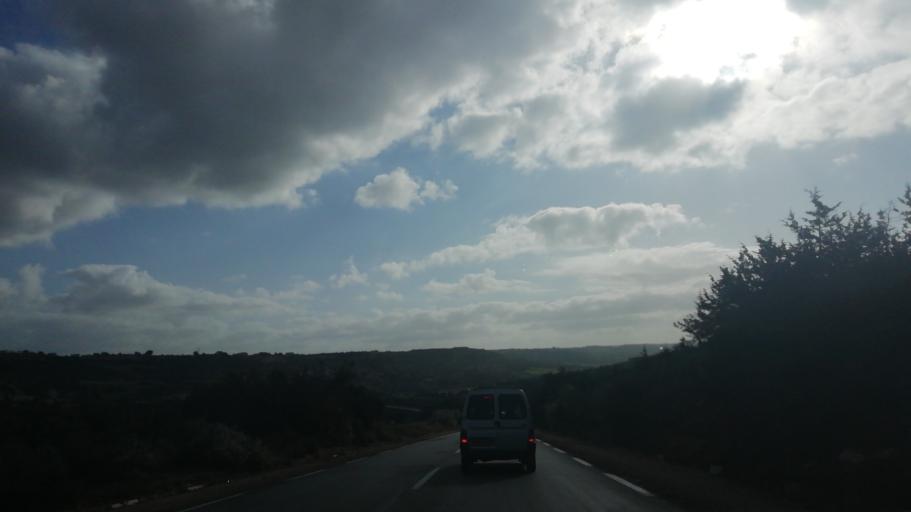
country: DZ
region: Relizane
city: Mazouna
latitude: 36.2385
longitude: 0.5338
